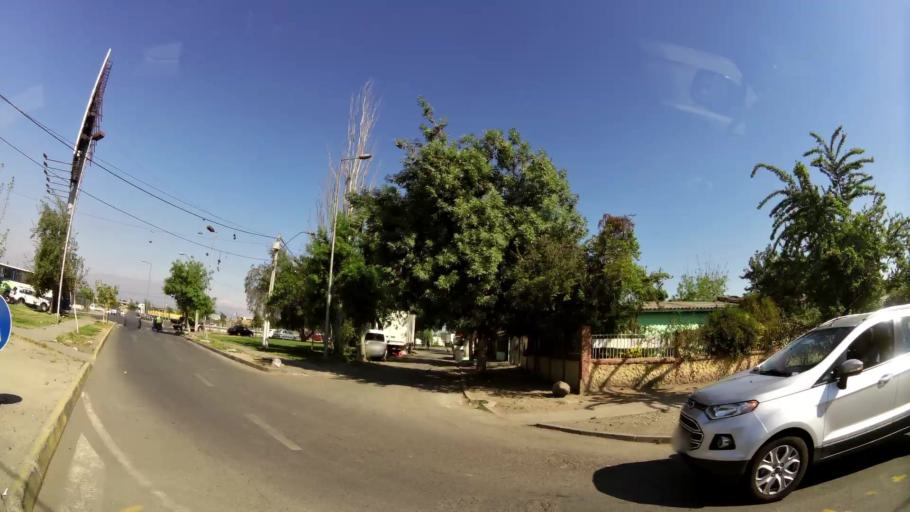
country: CL
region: Santiago Metropolitan
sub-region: Provincia de Santiago
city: La Pintana
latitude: -33.5375
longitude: -70.6106
